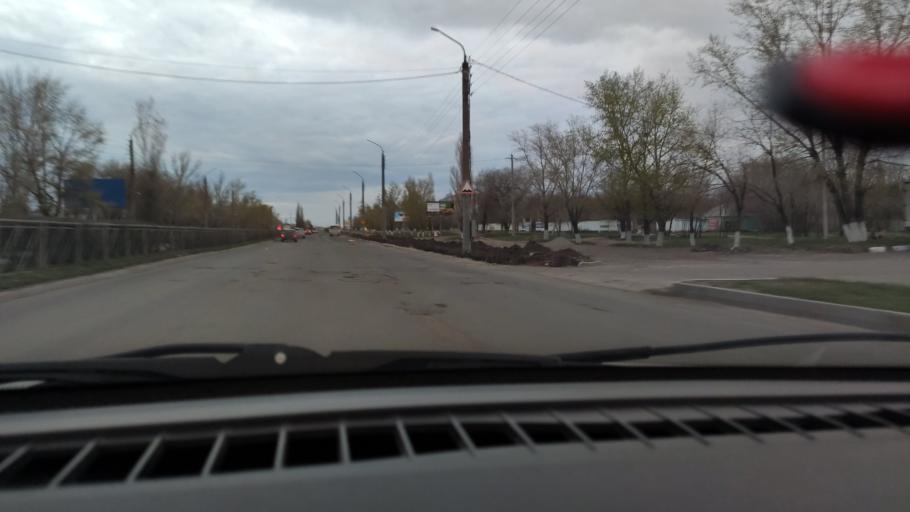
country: RU
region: Orenburg
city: Orenburg
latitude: 51.8191
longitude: 55.1077
